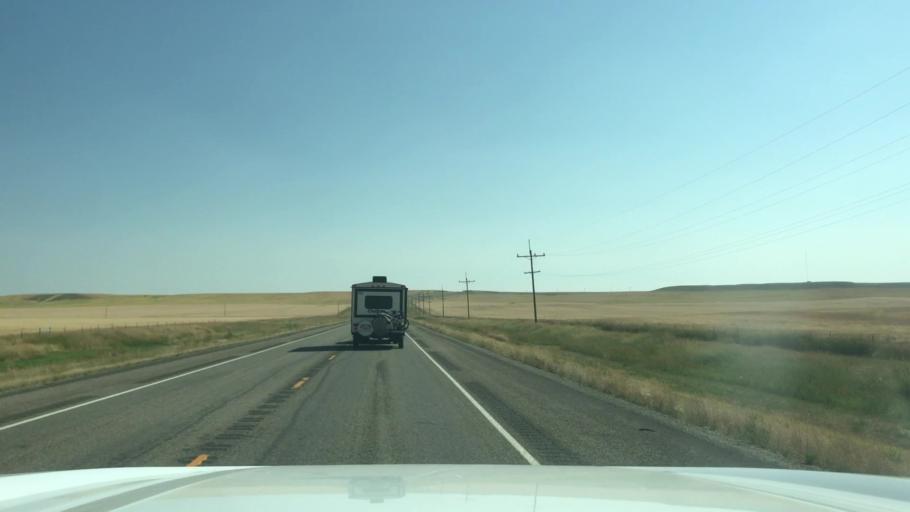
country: US
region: Montana
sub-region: Wheatland County
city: Harlowton
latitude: 46.4847
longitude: -109.7661
